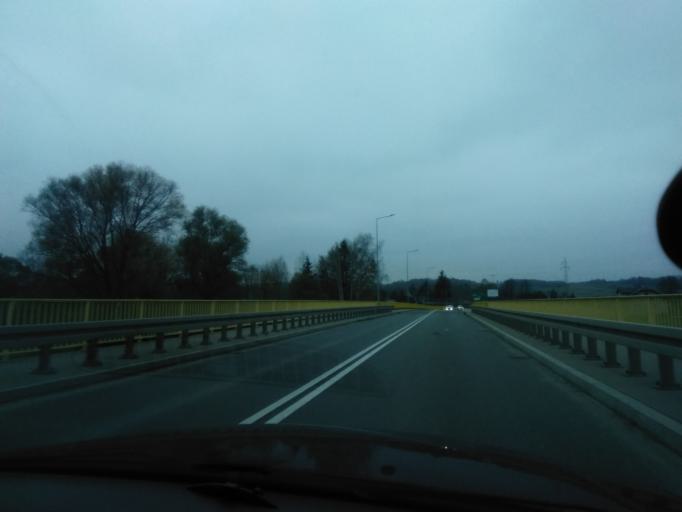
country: PL
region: Subcarpathian Voivodeship
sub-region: Powiat strzyzowski
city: Czudec
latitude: 49.9347
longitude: 21.8169
